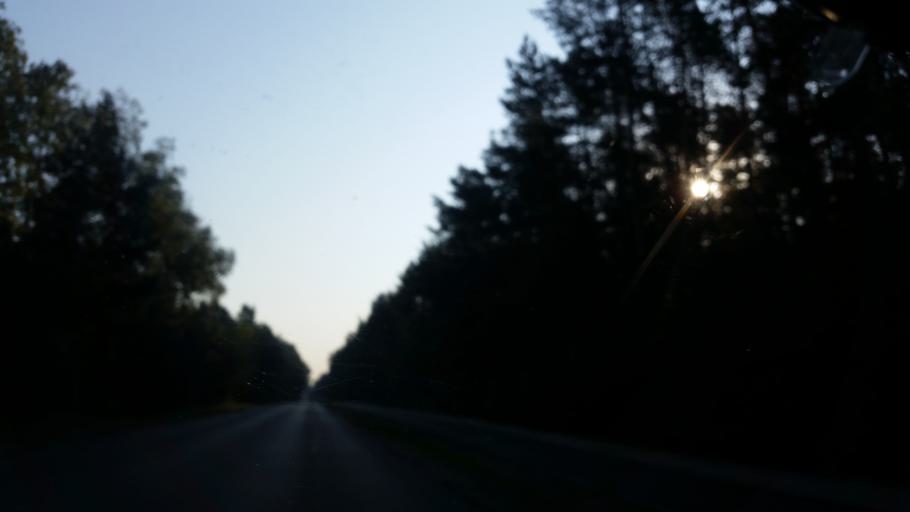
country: PL
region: Masovian Voivodeship
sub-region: Powiat otwocki
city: Jozefow
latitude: 52.1434
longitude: 21.1998
